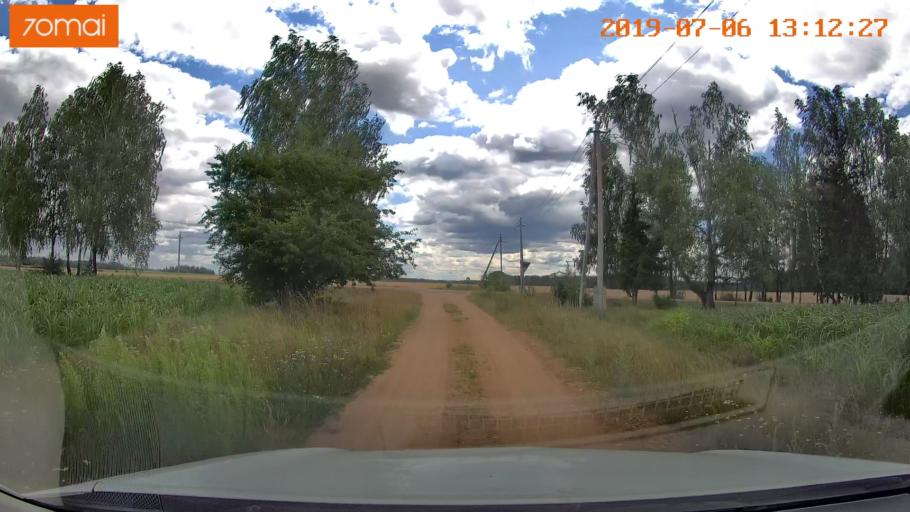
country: BY
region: Minsk
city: Enyerhyetykaw
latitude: 53.6588
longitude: 26.9935
